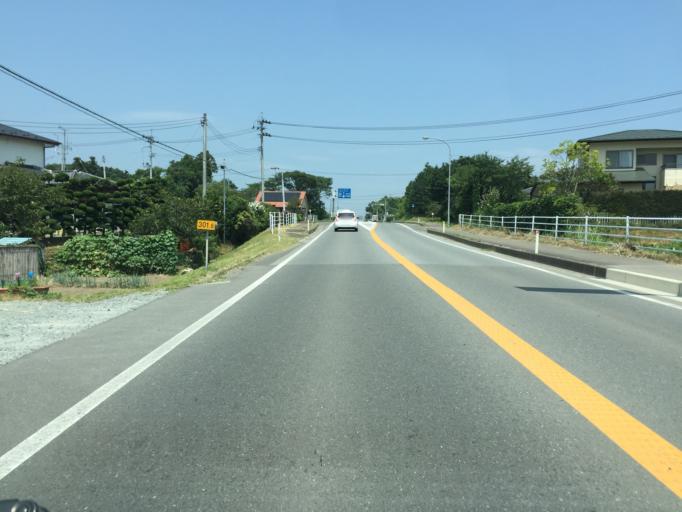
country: JP
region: Miyagi
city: Marumori
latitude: 37.8350
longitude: 140.9183
